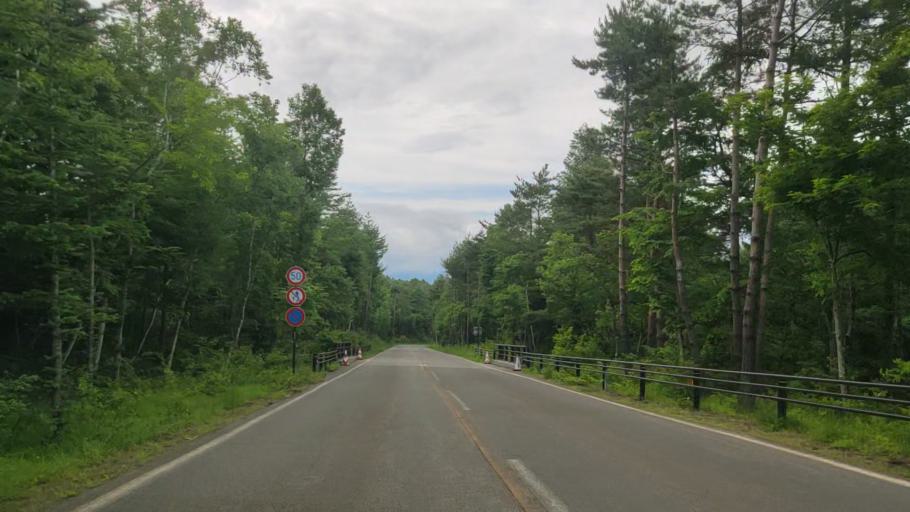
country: JP
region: Yamanashi
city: Fujikawaguchiko
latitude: 35.4307
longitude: 138.7383
